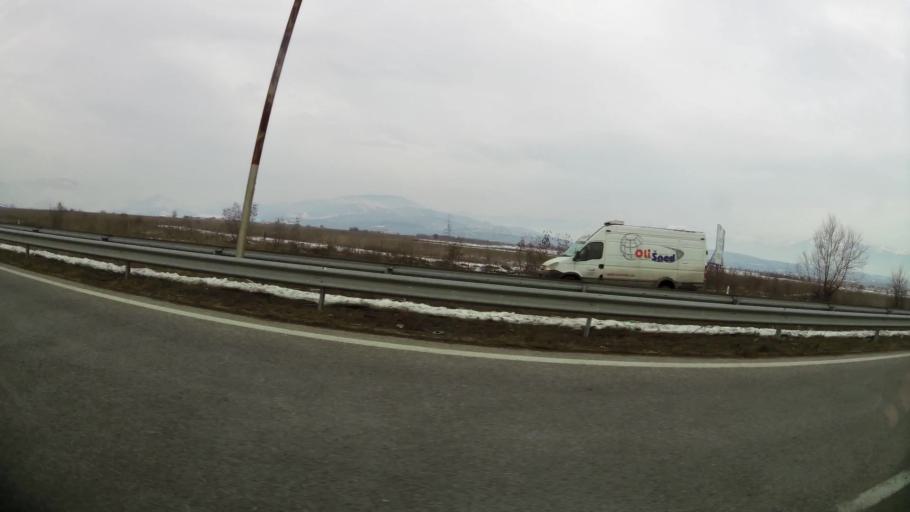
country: MK
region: Suto Orizari
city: Suto Orizare
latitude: 42.0530
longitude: 21.3887
